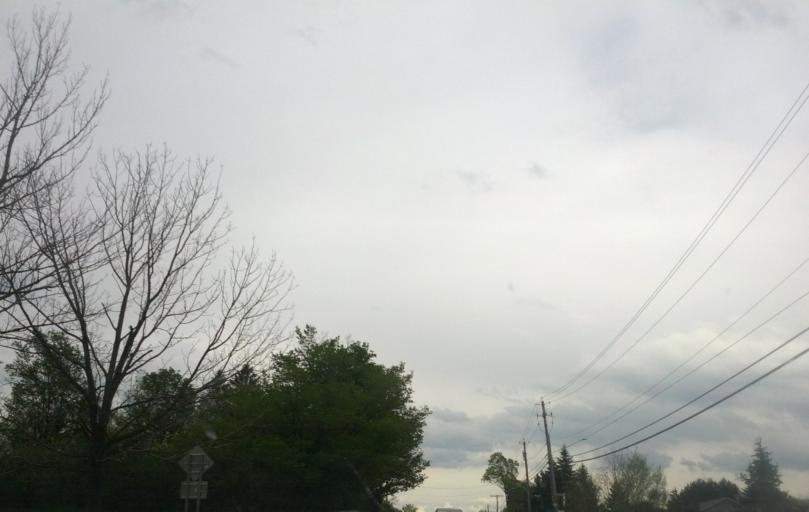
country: US
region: New York
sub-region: Onondaga County
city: Nedrow
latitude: 42.9975
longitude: -76.1162
